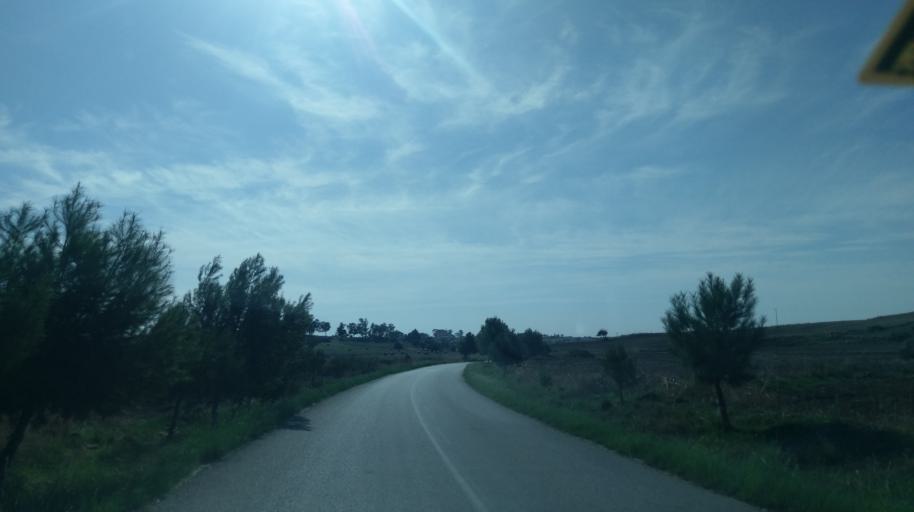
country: CY
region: Ammochostos
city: Trikomo
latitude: 35.3767
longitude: 34.0006
